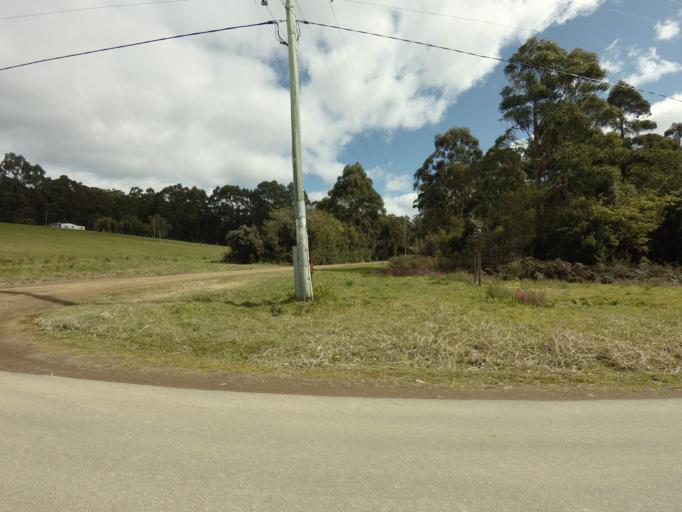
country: AU
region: Tasmania
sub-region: Huon Valley
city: Geeveston
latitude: -43.4233
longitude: 146.9725
